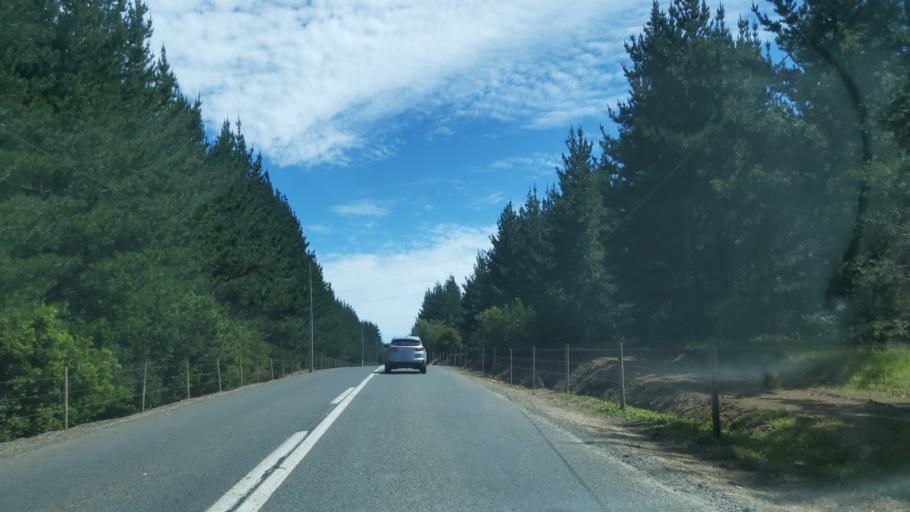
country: CL
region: Maule
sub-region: Provincia de Talca
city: Constitucion
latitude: -35.5287
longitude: -72.5405
